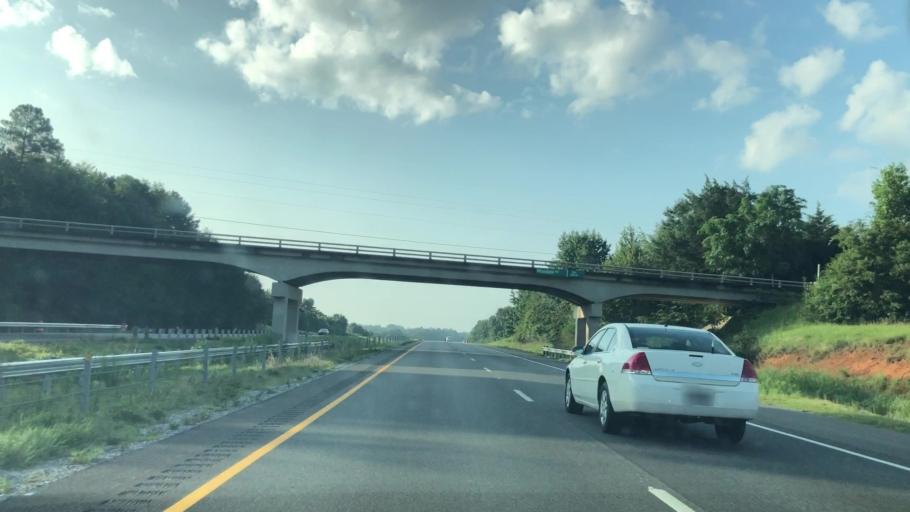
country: US
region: Alabama
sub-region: Chilton County
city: Clanton
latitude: 32.8654
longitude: -86.6077
